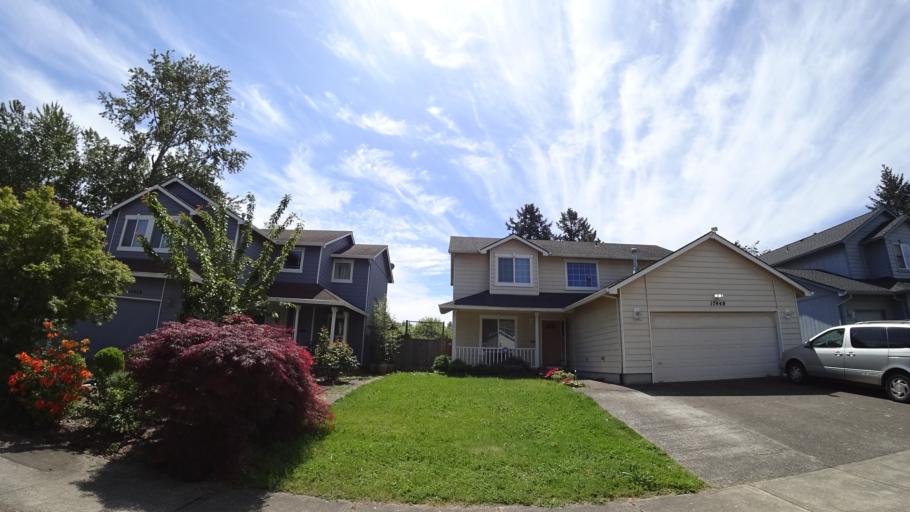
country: US
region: Oregon
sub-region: Washington County
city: Aloha
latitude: 45.4884
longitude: -122.8566
